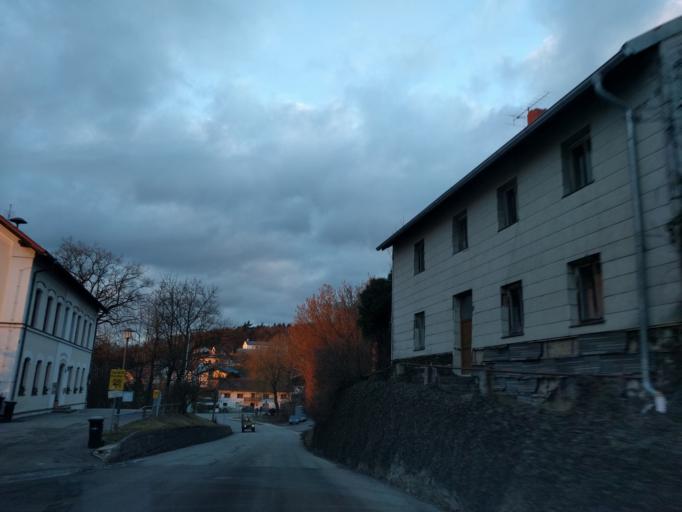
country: DE
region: Bavaria
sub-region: Lower Bavaria
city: Hofkirchen
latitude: 48.6945
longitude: 13.1207
